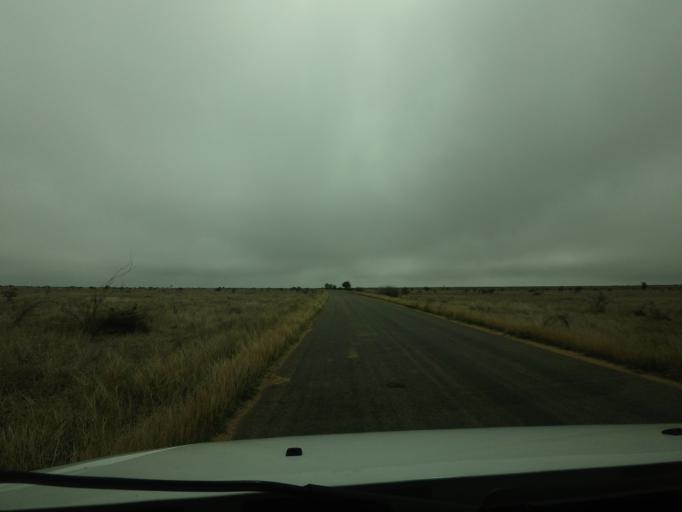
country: ZA
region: Limpopo
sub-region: Mopani District Municipality
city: Phalaborwa
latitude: -24.2313
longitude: 31.7211
